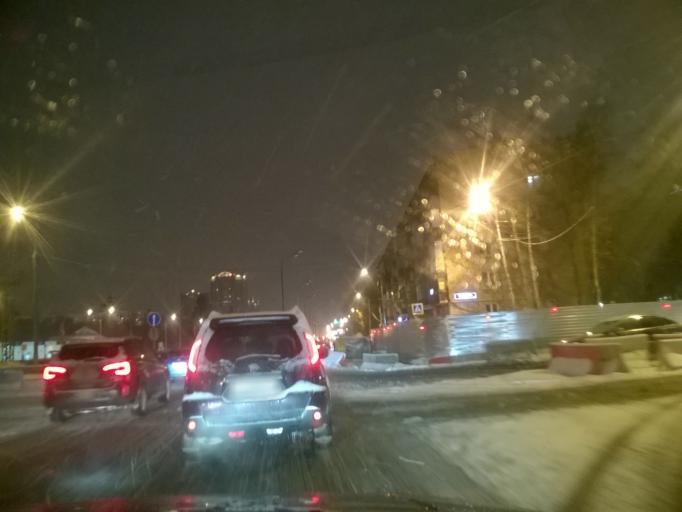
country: RU
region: Moscow
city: Davydkovo
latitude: 55.7179
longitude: 37.4518
